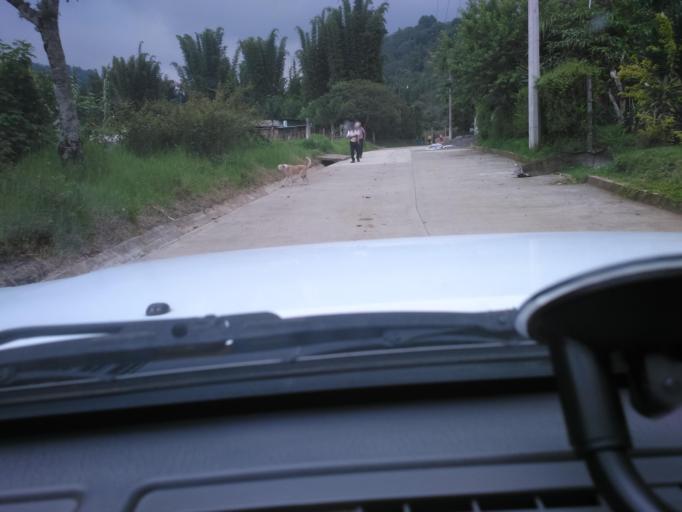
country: MX
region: Veracruz
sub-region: Mariano Escobedo
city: Chicola
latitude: 18.9116
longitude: -97.1099
